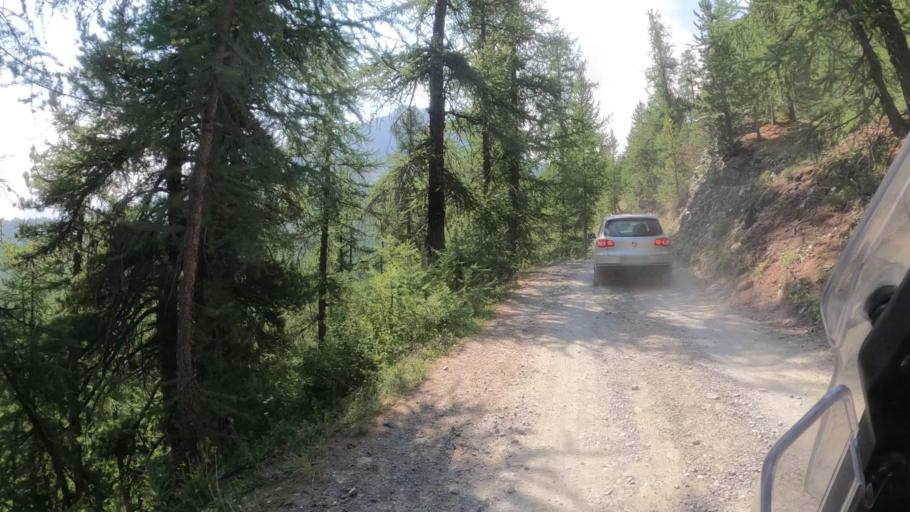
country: IT
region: Piedmont
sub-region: Provincia di Torino
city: Cesana Torinese
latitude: 44.9123
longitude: 6.7994
